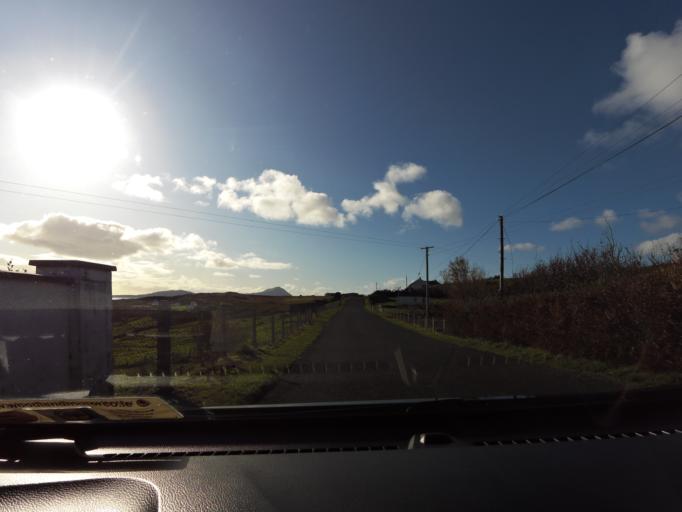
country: IE
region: Connaught
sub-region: Maigh Eo
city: Belmullet
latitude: 53.8683
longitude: -9.8971
